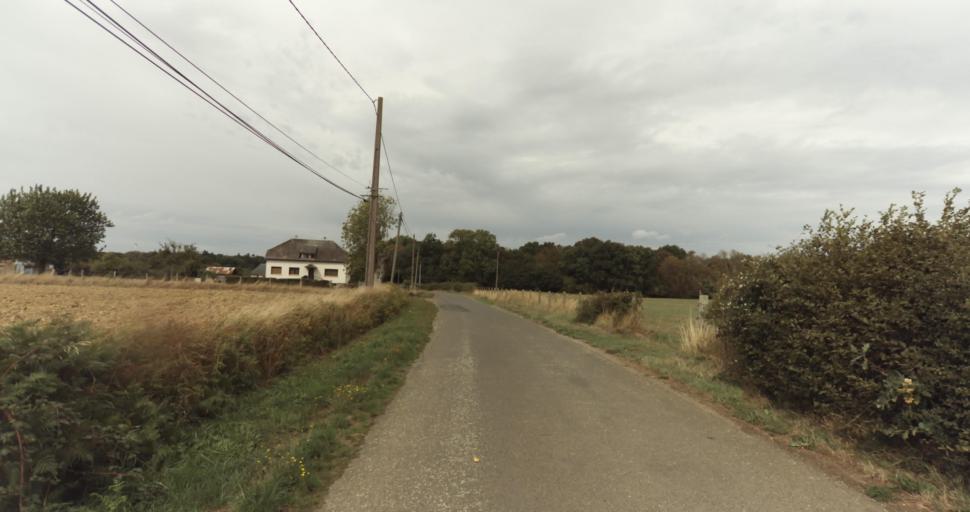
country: FR
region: Lower Normandy
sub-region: Departement du Calvados
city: Orbec
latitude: 48.9446
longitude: 0.3763
